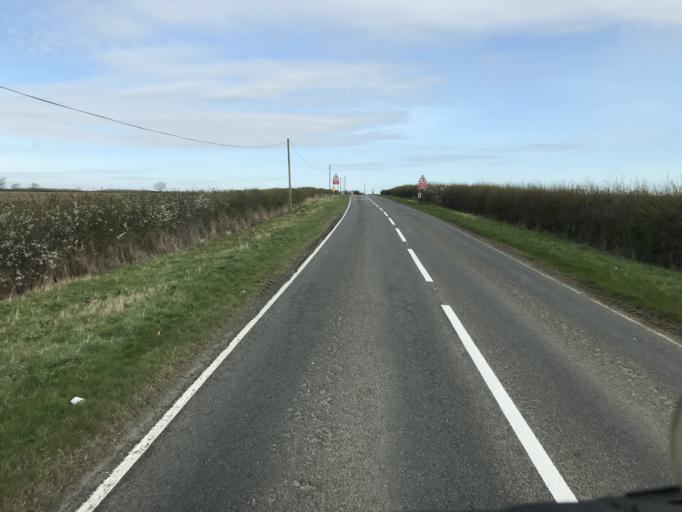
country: GB
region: England
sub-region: Lincolnshire
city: Market Rasen
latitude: 53.3927
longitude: -0.4055
